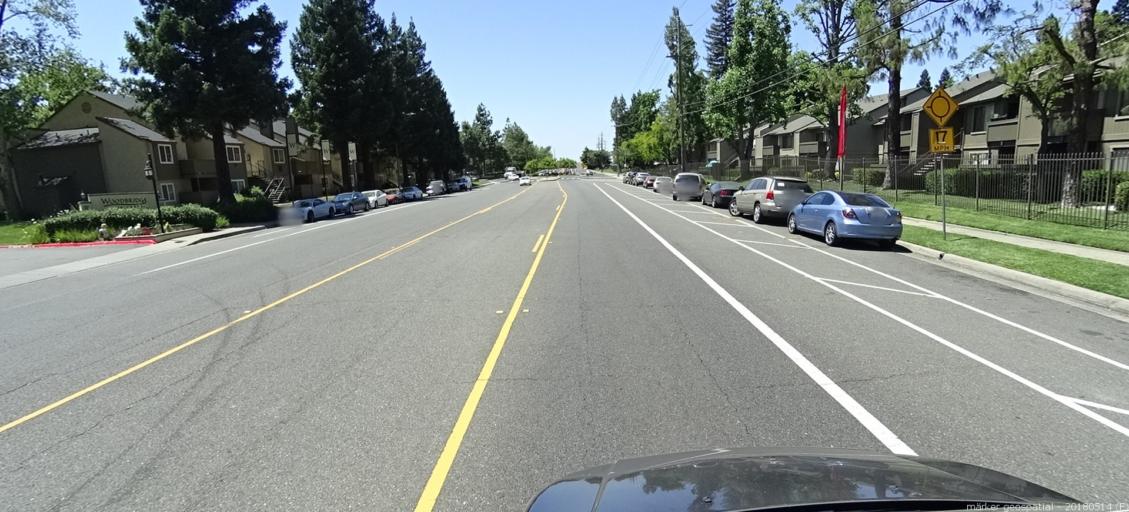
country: US
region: California
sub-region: Sacramento County
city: Sacramento
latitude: 38.6275
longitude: -121.5068
